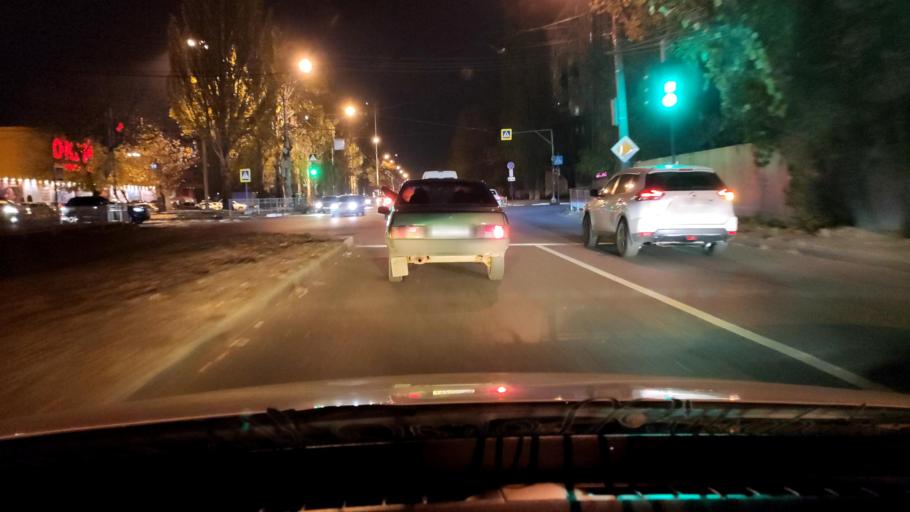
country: RU
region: Voronezj
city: Voronezh
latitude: 51.7038
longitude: 39.1955
